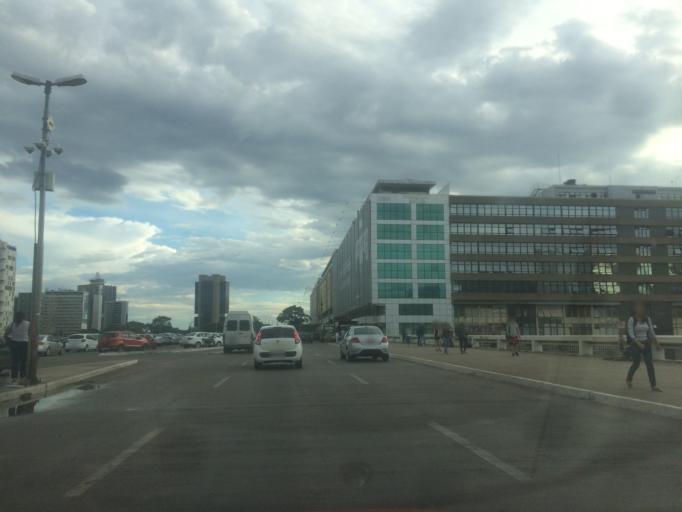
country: BR
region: Federal District
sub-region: Brasilia
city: Brasilia
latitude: -15.7940
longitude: -47.8835
